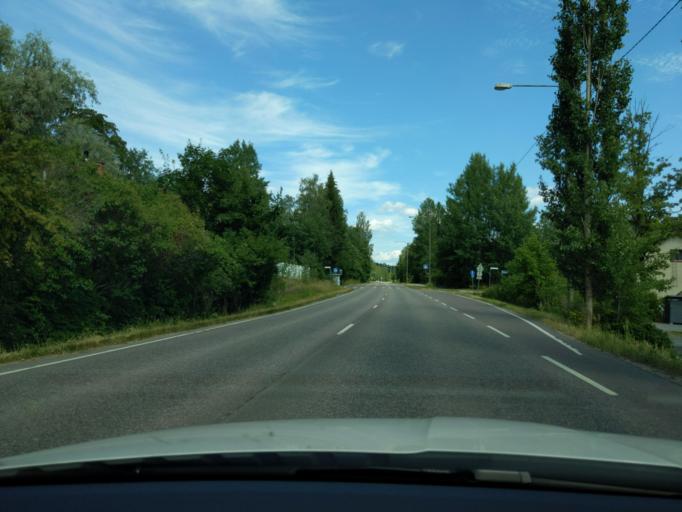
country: FI
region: Paijanne Tavastia
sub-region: Lahti
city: Lahti
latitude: 61.0187
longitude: 25.7186
